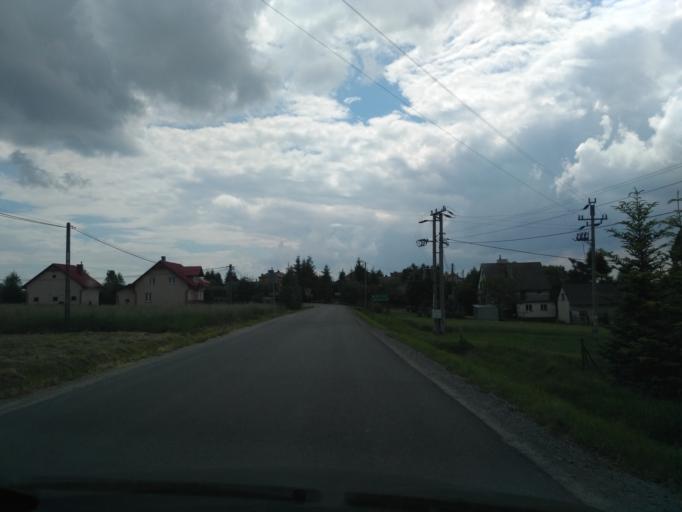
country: PL
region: Subcarpathian Voivodeship
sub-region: Powiat rzeszowski
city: Hyzne
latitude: 49.9329
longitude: 22.1840
